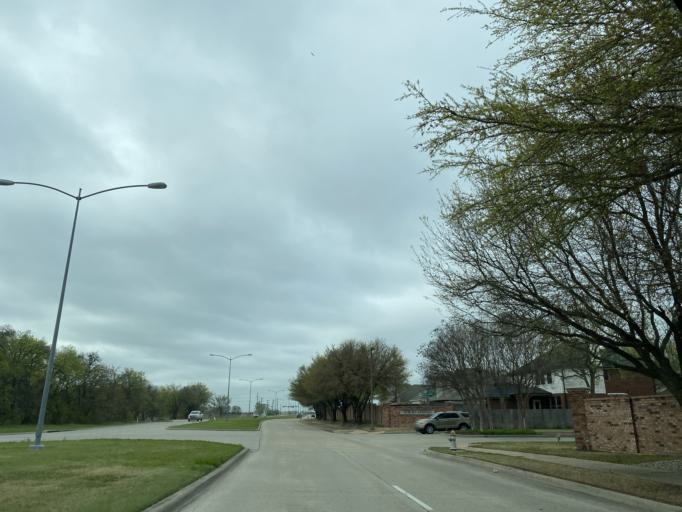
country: US
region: Texas
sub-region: Collin County
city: Lucas
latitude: 33.1040
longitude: -96.6205
